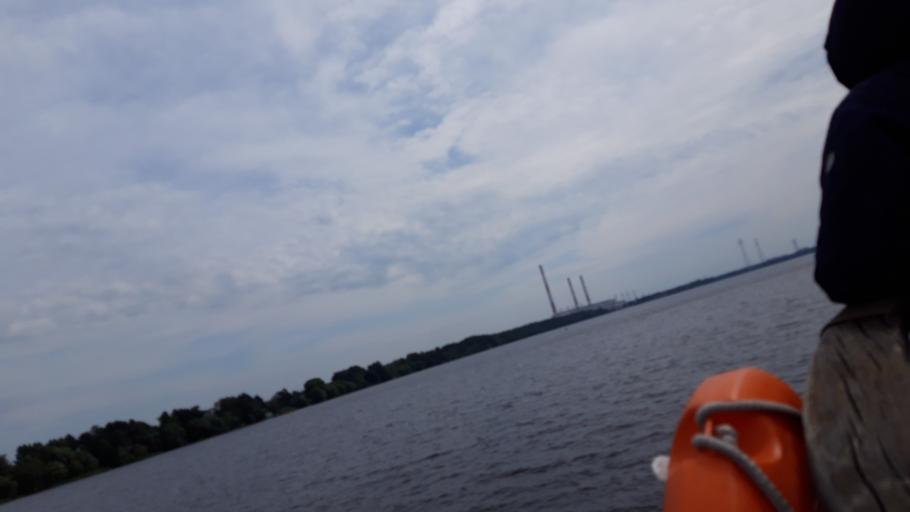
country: RU
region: Tverskaya
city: Konakovo
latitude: 56.7586
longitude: 36.7381
